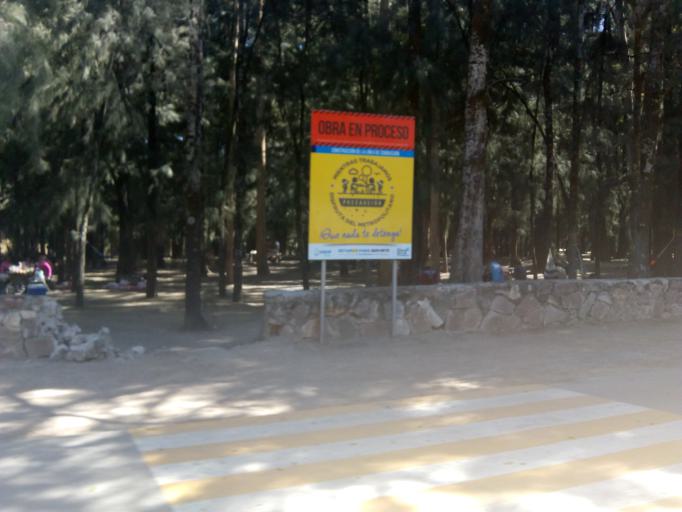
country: MX
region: Guanajuato
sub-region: Leon
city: La Ermita
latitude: 21.1728
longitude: -101.6938
